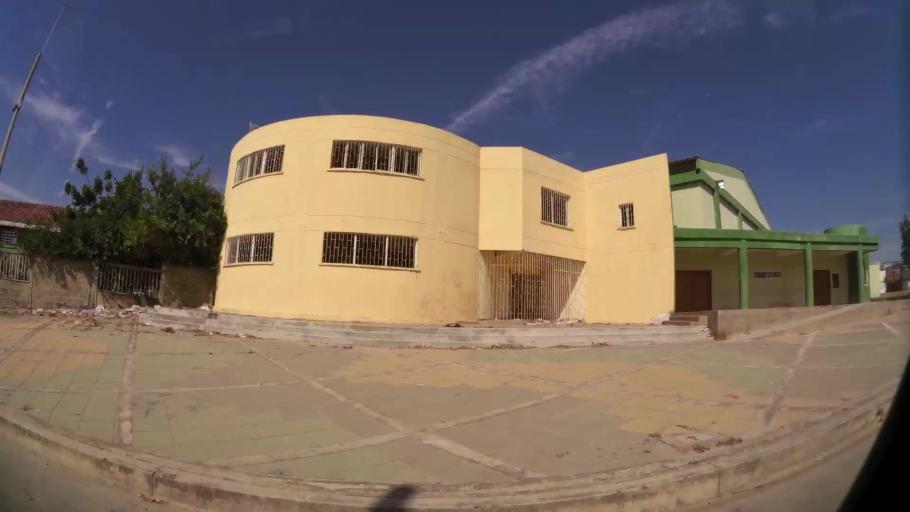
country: CO
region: Atlantico
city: Barranquilla
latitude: 10.9304
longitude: -74.8206
